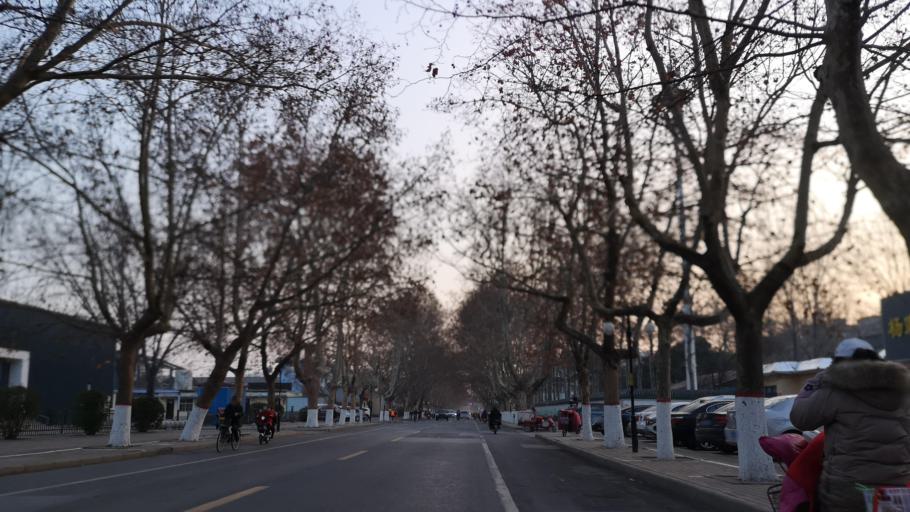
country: CN
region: Henan Sheng
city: Zhongyuanlu
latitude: 35.7719
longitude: 115.0752
